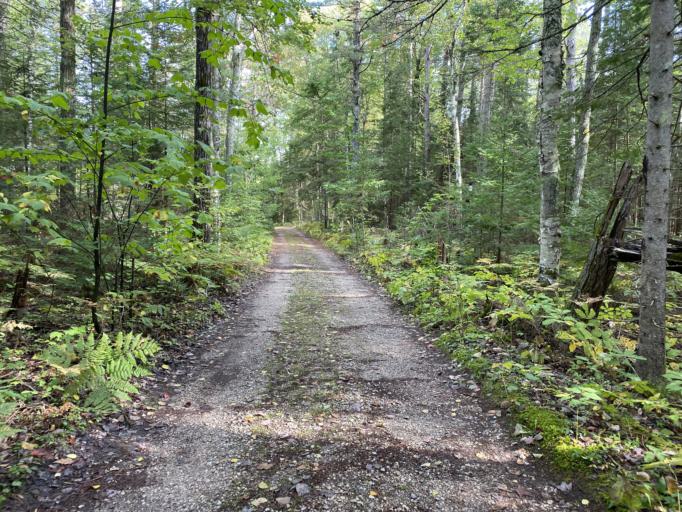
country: US
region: Michigan
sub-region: Mackinac County
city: Saint Ignace
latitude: 45.7498
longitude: -84.8784
